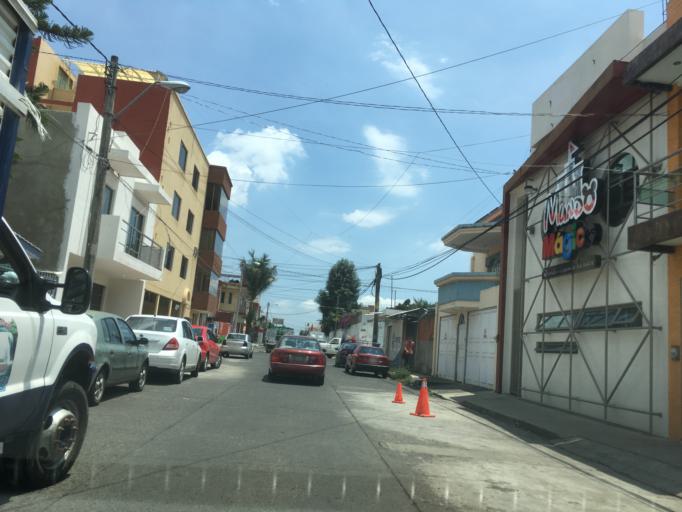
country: MX
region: Michoacan
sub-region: Uruapan
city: Uruapan
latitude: 19.4123
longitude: -102.0545
